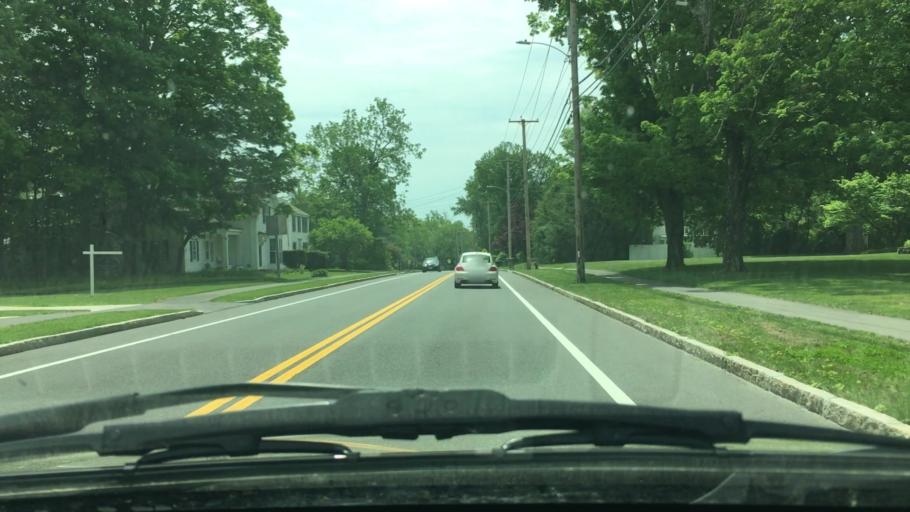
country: US
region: Massachusetts
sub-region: Hampshire County
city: Belchertown
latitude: 42.2756
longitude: -72.4000
